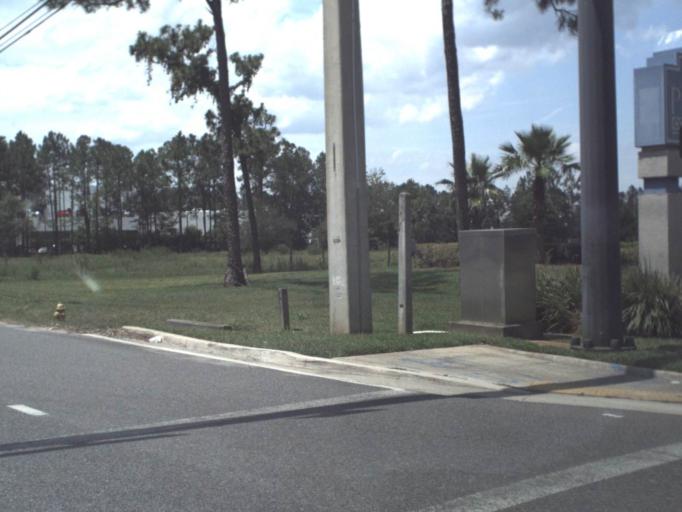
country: US
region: Florida
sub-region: Saint Johns County
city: Fruit Cove
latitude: 30.1591
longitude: -81.5325
